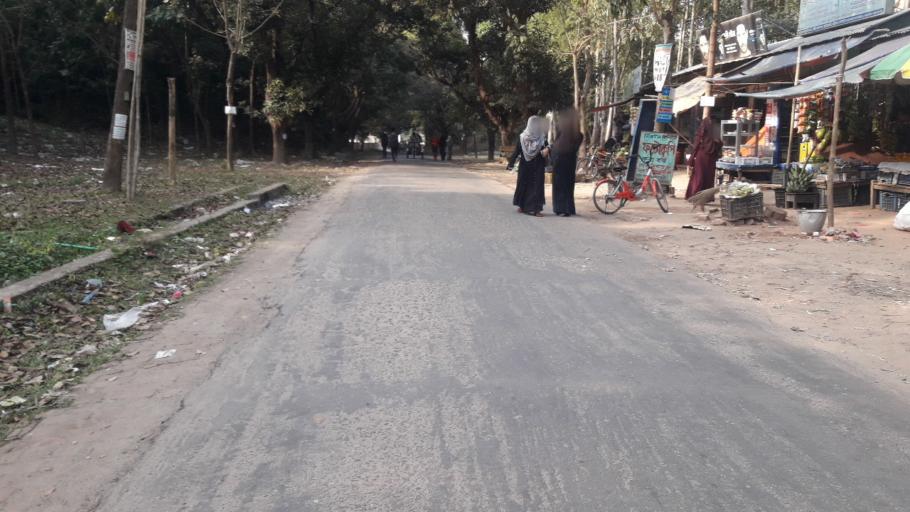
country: BD
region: Chittagong
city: Chittagong
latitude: 22.4689
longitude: 91.7939
